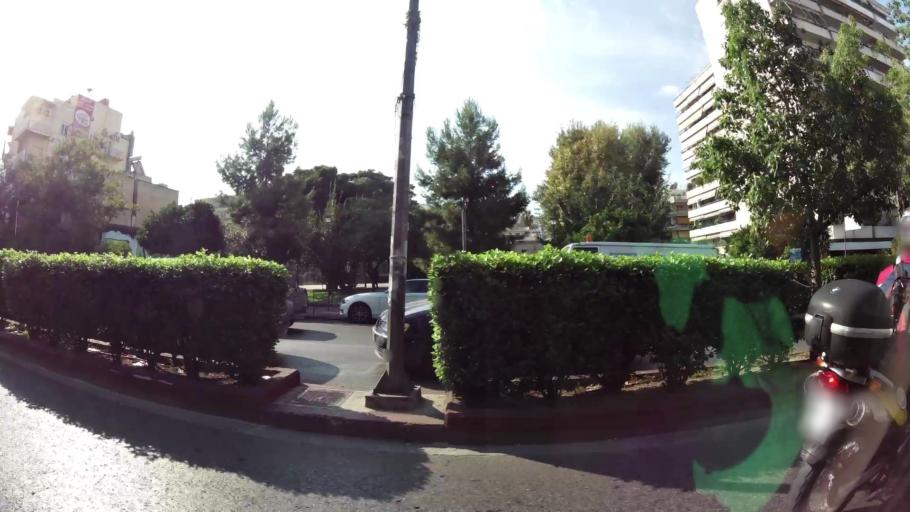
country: GR
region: Attica
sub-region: Nomarchia Athinas
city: Galatsi
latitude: 38.0133
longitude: 23.7520
